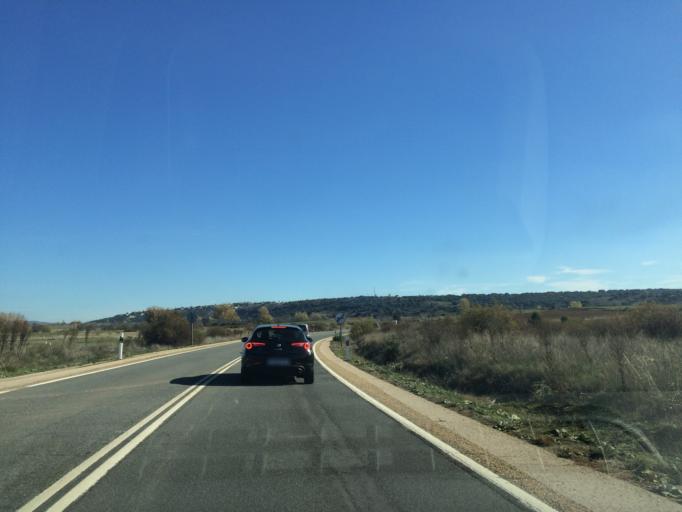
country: ES
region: Madrid
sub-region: Provincia de Madrid
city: Venturada
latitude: 40.7823
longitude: -3.6386
